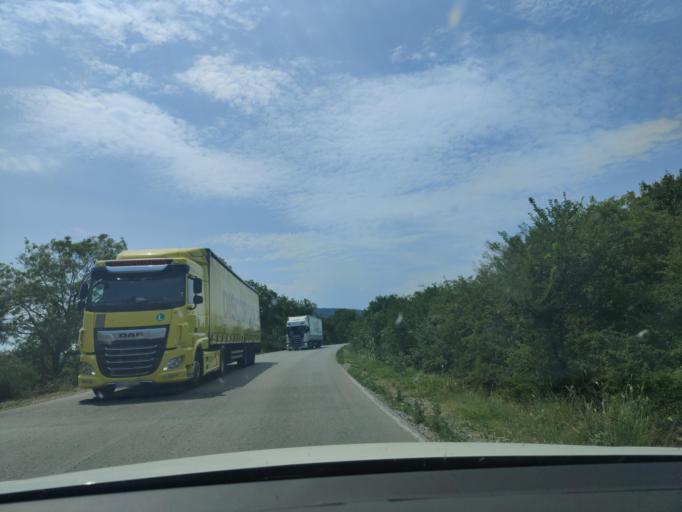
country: BG
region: Montana
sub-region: Obshtina Montana
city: Montana
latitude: 43.4776
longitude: 23.0912
